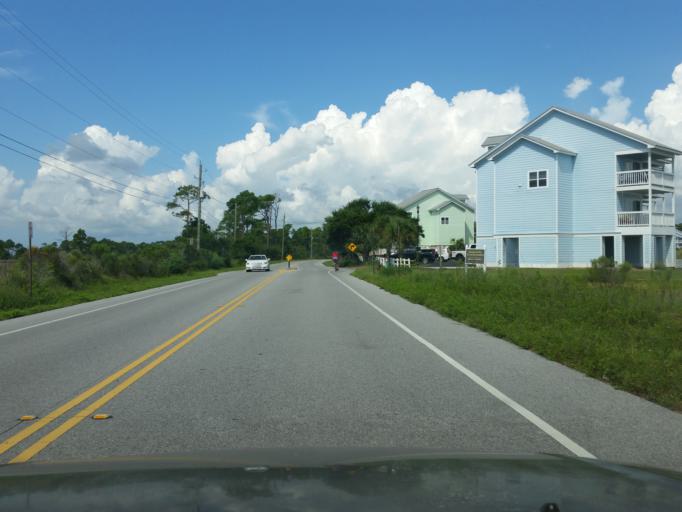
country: US
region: Alabama
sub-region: Baldwin County
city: Orange Beach
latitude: 30.3141
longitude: -87.4730
